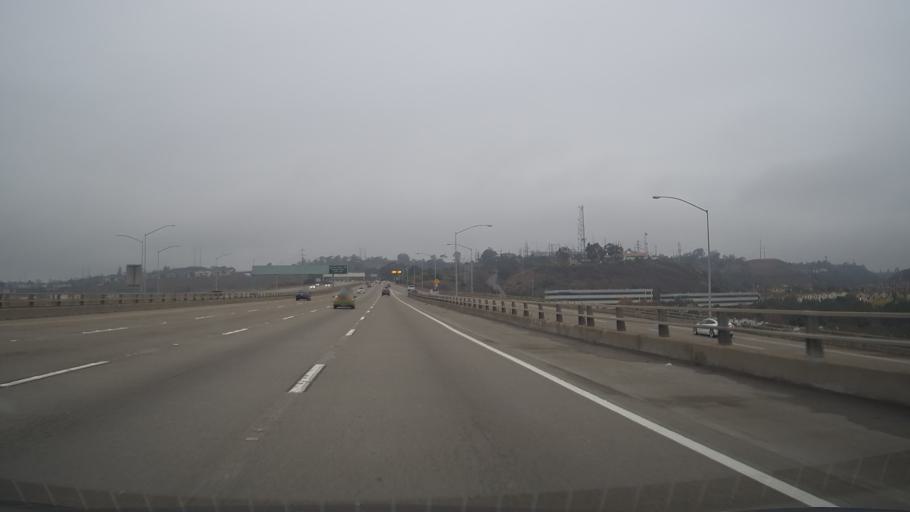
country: US
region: California
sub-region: San Diego County
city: San Diego
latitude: 32.7738
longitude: -117.1327
